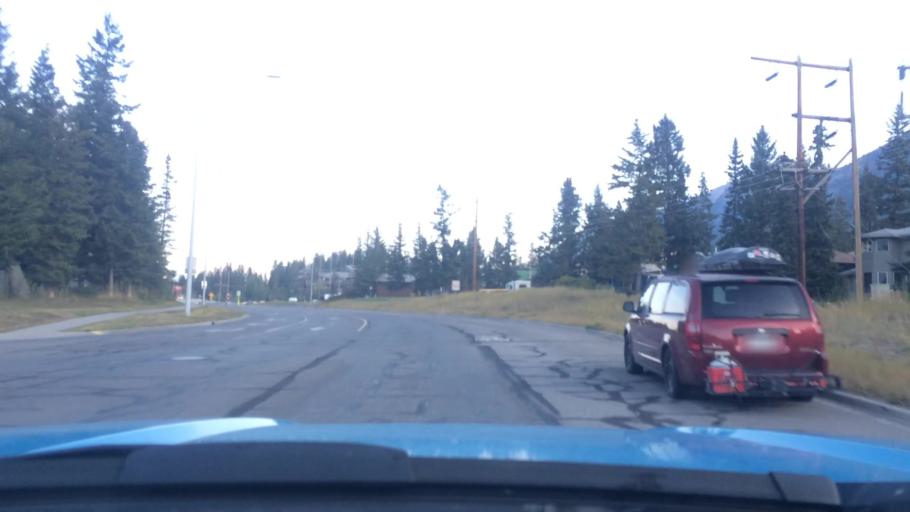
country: CA
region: Alberta
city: Canmore
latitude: 51.0846
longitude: -115.3246
